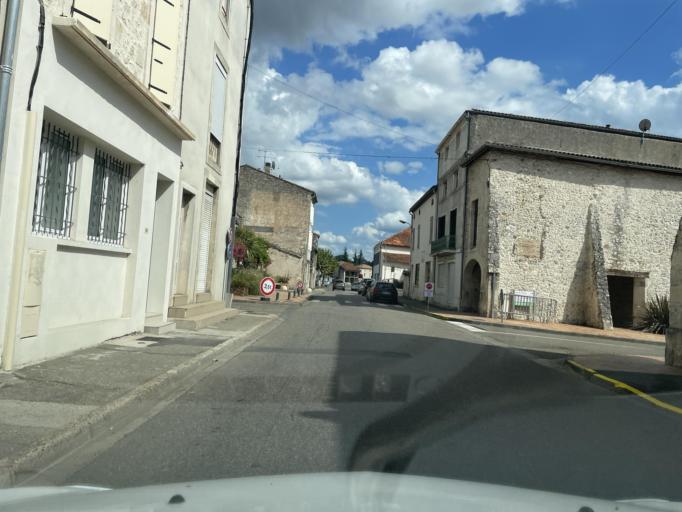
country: FR
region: Aquitaine
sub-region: Departement du Lot-et-Garonne
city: Casteljaloux
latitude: 44.3135
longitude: 0.0879
